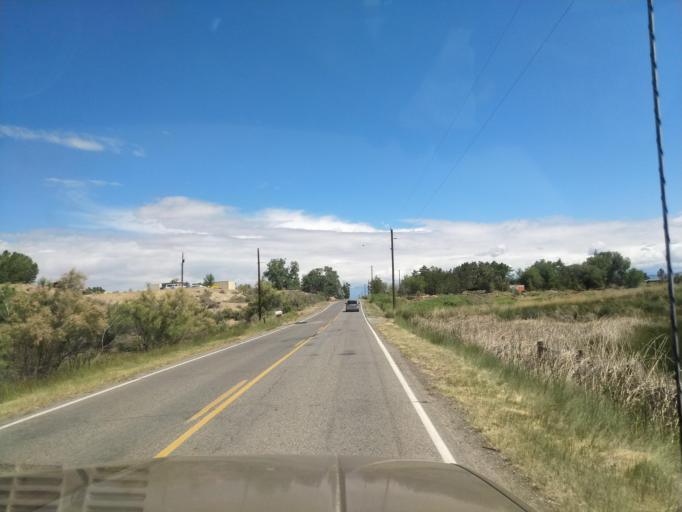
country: US
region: Colorado
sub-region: Mesa County
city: Redlands
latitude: 39.1287
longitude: -108.6080
